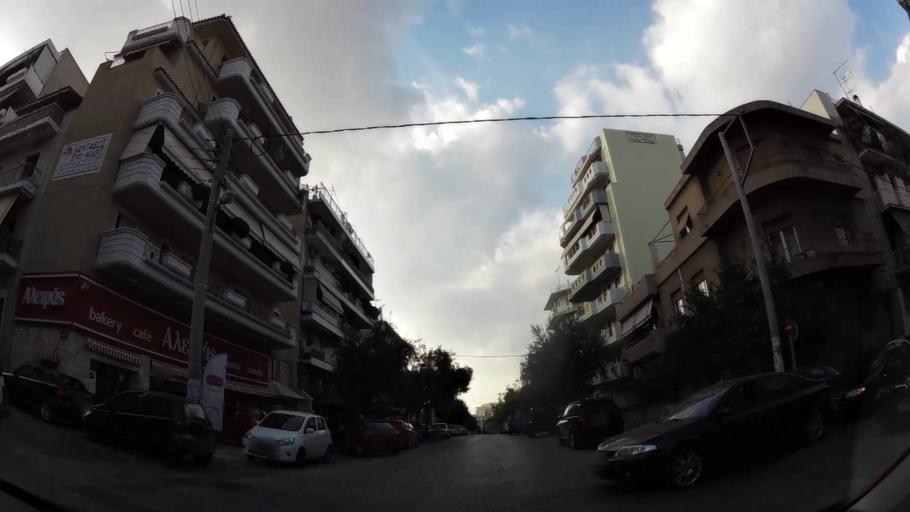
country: GR
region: Attica
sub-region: Nomarchia Athinas
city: Dhafni
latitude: 37.9534
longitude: 23.7247
